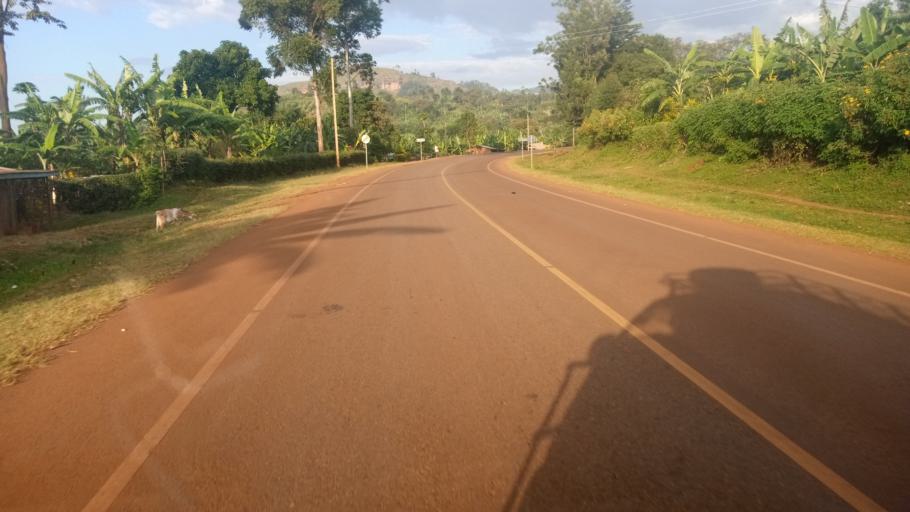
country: UG
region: Eastern Region
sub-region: Kapchorwa District
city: Kapchorwa
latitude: 1.3223
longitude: 34.3451
